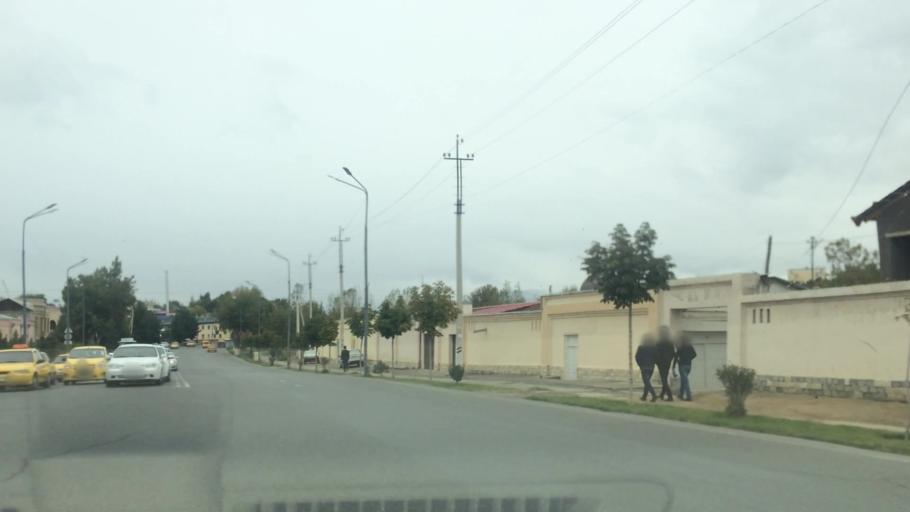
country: UZ
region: Samarqand
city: Samarqand
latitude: 39.6576
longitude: 66.9709
